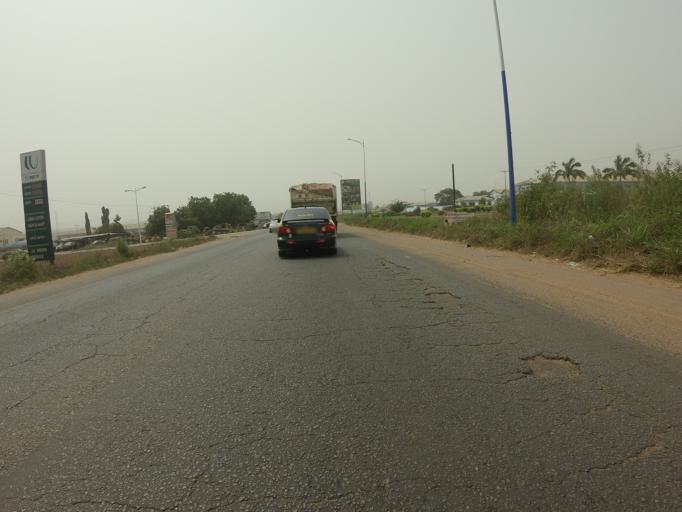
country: GH
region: Greater Accra
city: Tema
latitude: 5.7255
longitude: 0.0225
